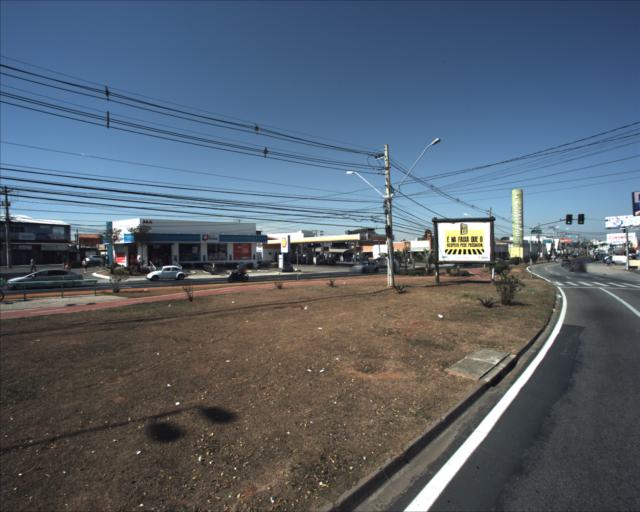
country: BR
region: Sao Paulo
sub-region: Sorocaba
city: Sorocaba
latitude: -23.4635
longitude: -47.4795
